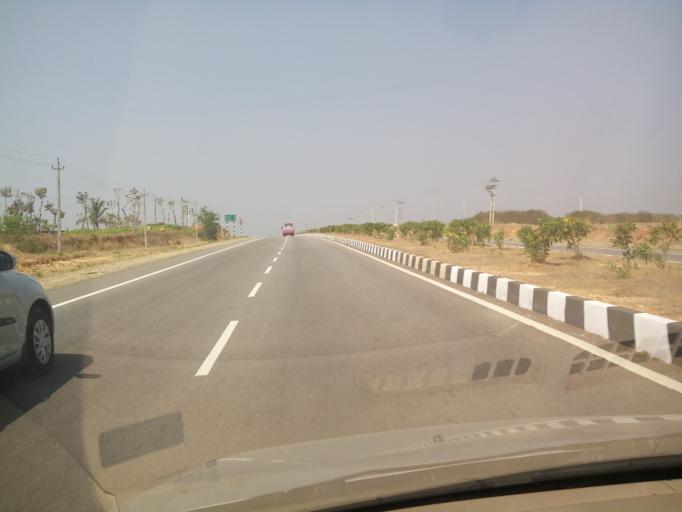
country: IN
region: Karnataka
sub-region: Hassan
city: Shravanabelagola
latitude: 12.9215
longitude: 76.4875
